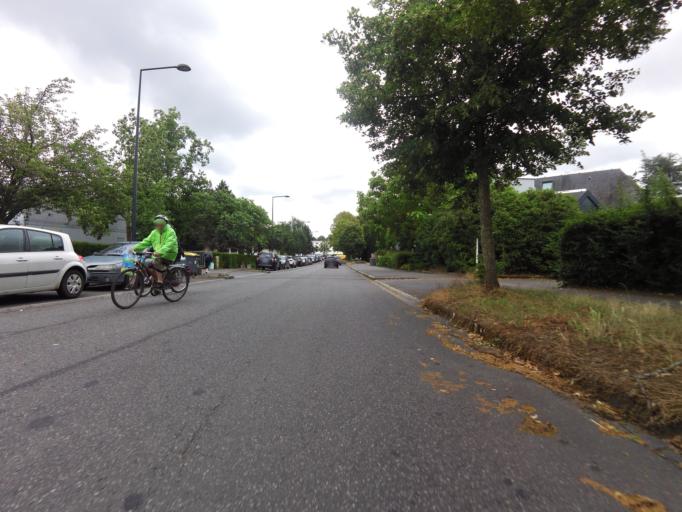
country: FR
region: Brittany
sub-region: Departement d'Ille-et-Vilaine
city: Rennes
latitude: 48.0880
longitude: -1.6721
